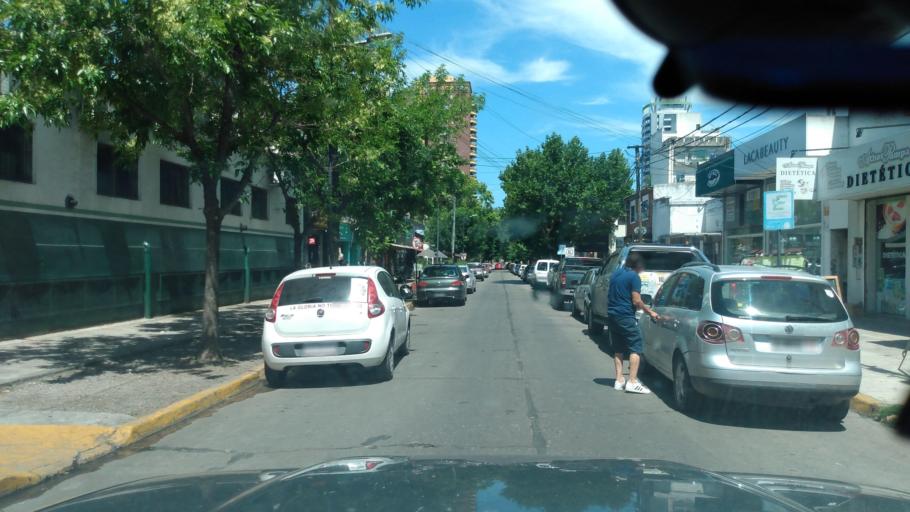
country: AR
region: Buenos Aires
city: Hurlingham
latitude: -34.5424
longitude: -58.7083
